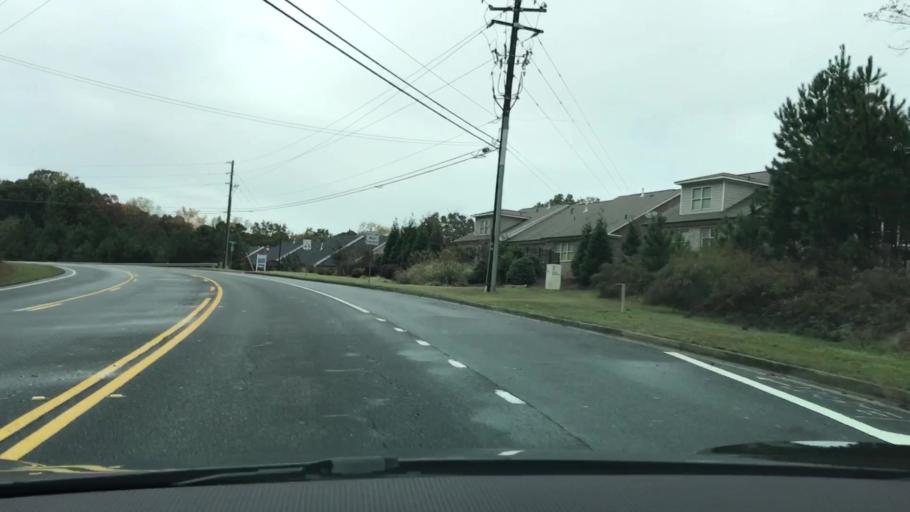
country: US
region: Georgia
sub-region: Gwinnett County
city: Suwanee
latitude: 34.0806
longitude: -84.1272
